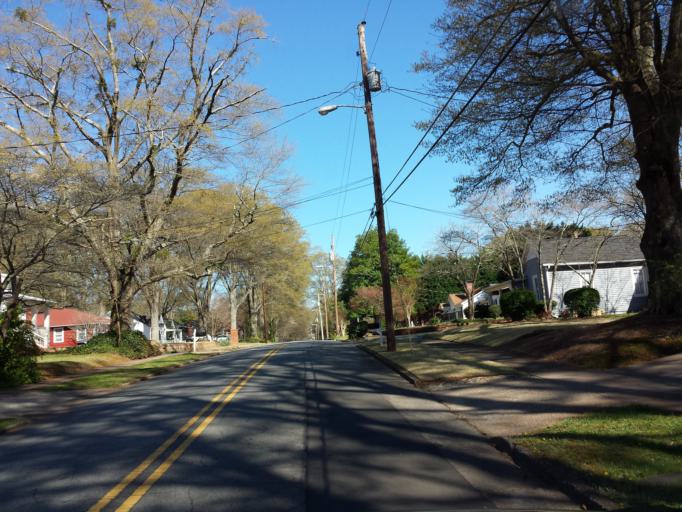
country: US
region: Georgia
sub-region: Cobb County
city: Marietta
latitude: 33.9593
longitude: -84.5623
